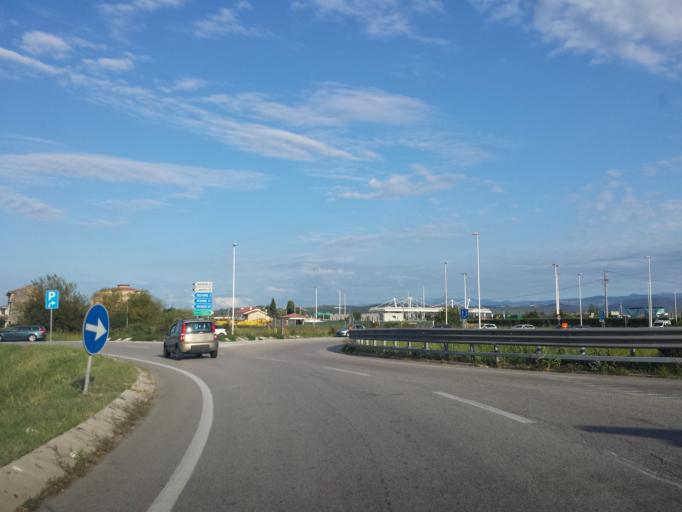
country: IT
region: Veneto
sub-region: Provincia di Verona
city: Soave
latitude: 45.4047
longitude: 11.2552
